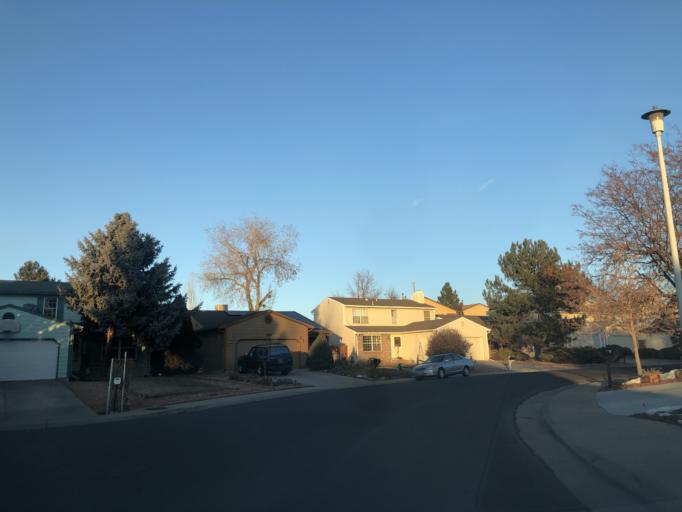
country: US
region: Colorado
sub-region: Adams County
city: Aurora
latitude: 39.7058
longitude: -104.8047
